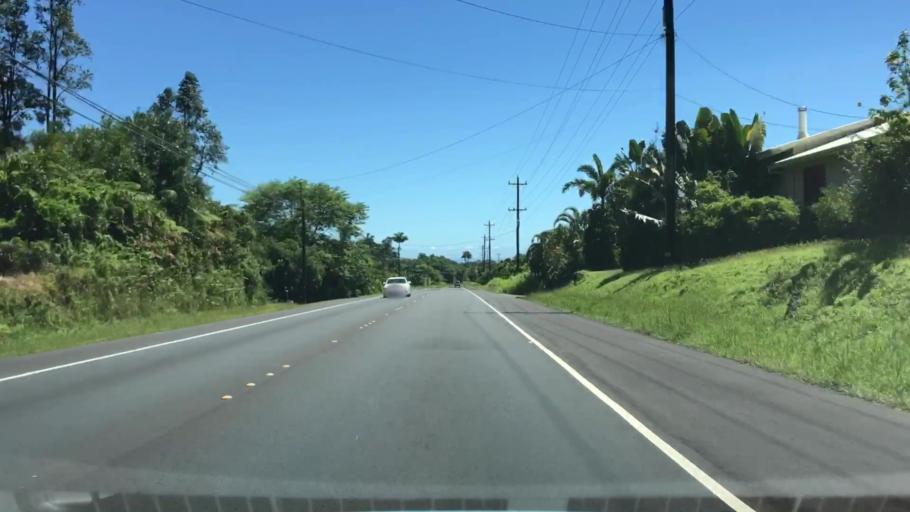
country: US
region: Hawaii
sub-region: Hawaii County
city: Mountain View
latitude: 19.5697
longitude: -155.0804
